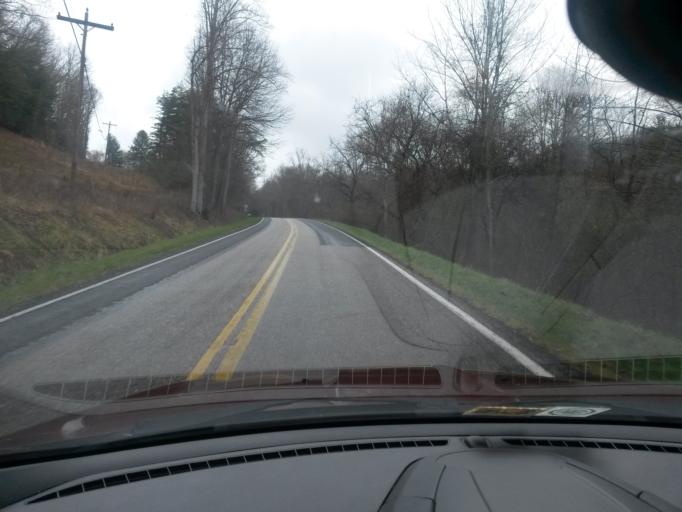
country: US
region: Virginia
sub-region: Bath County
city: Warm Springs
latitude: 37.9327
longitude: -79.7063
